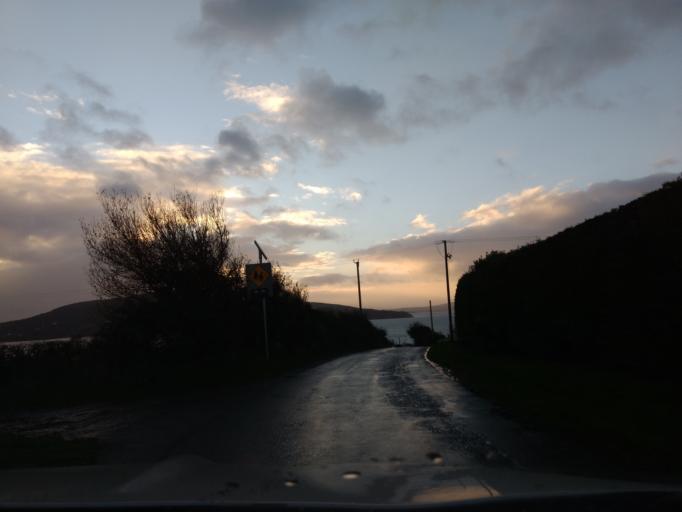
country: IE
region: Ulster
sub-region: County Donegal
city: Buncrana
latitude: 55.0969
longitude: -7.5424
